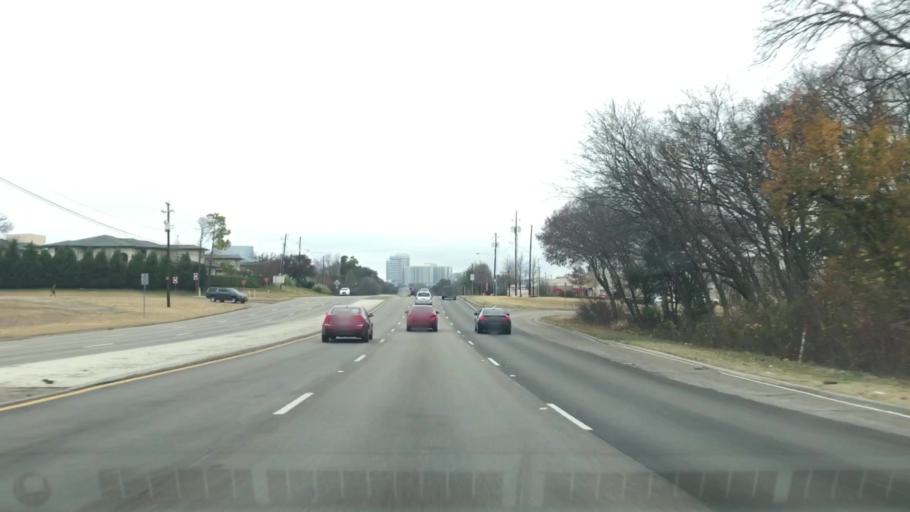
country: US
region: Texas
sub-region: Dallas County
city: Highland Park
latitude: 32.8597
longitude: -96.7539
